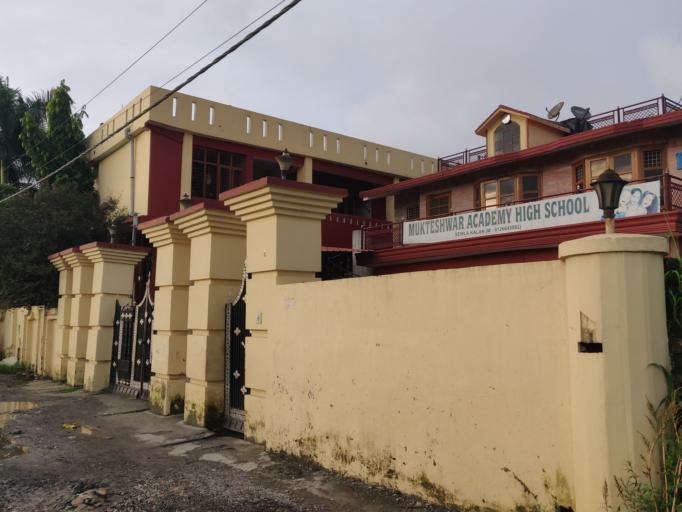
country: IN
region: Uttarakhand
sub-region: Dehradun
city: Clement Town
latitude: 30.3002
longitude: 77.9978
